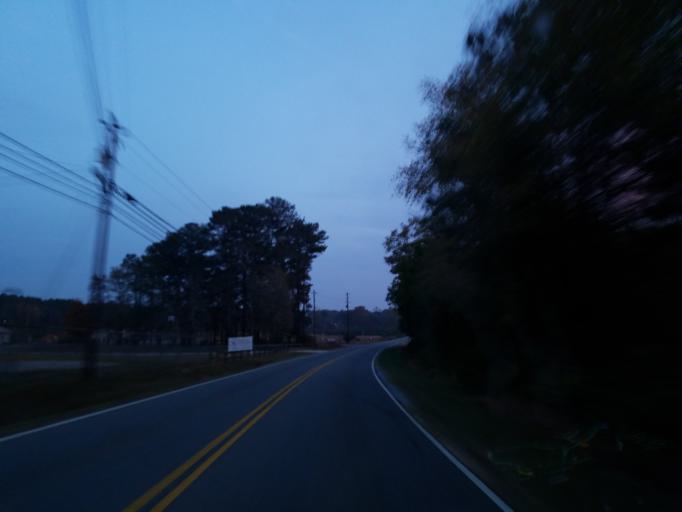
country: US
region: Georgia
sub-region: Pickens County
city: Jasper
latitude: 34.4808
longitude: -84.4490
